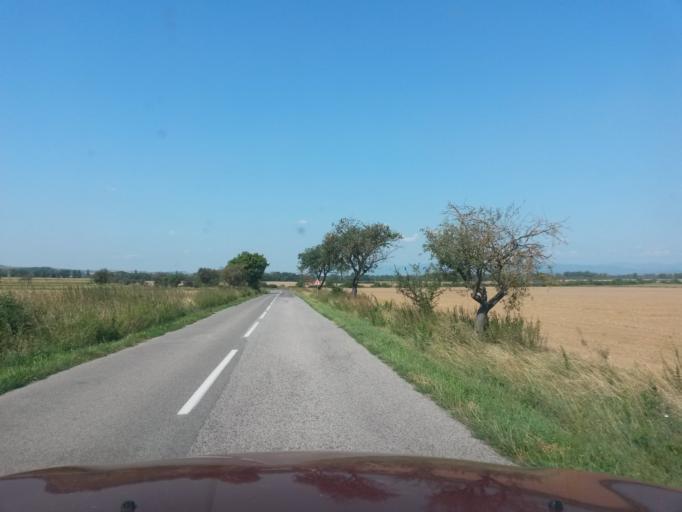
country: HU
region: Borsod-Abauj-Zemplen
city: Gonc
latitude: 48.5348
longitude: 21.1711
